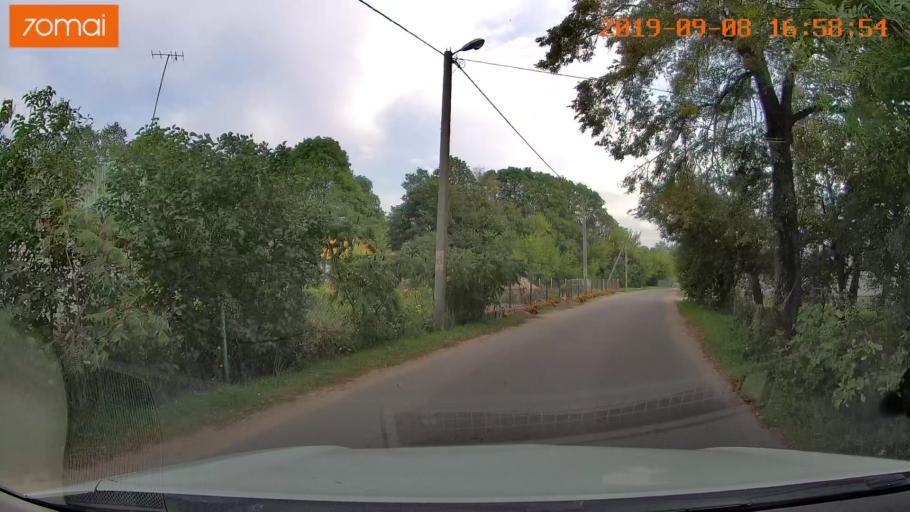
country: BY
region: Grodnenskaya
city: Hrodna
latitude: 53.7246
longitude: 23.9322
